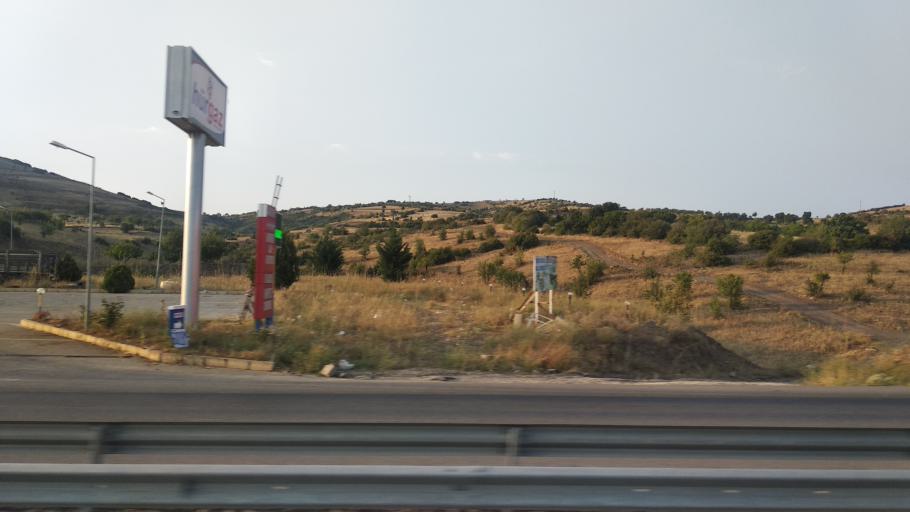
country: TR
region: Manisa
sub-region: Kula
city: Kula
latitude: 38.5677
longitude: 28.5715
